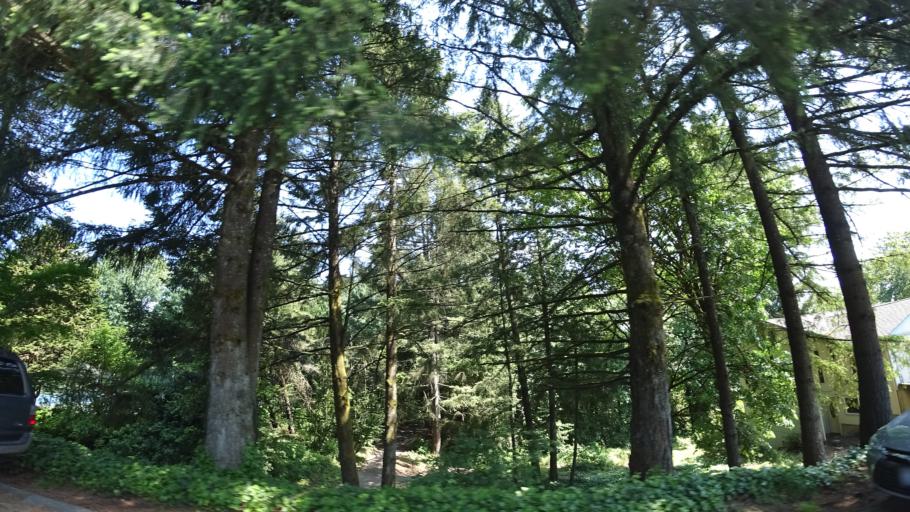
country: US
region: Oregon
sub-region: Clackamas County
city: Lake Oswego
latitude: 45.4321
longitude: -122.7151
